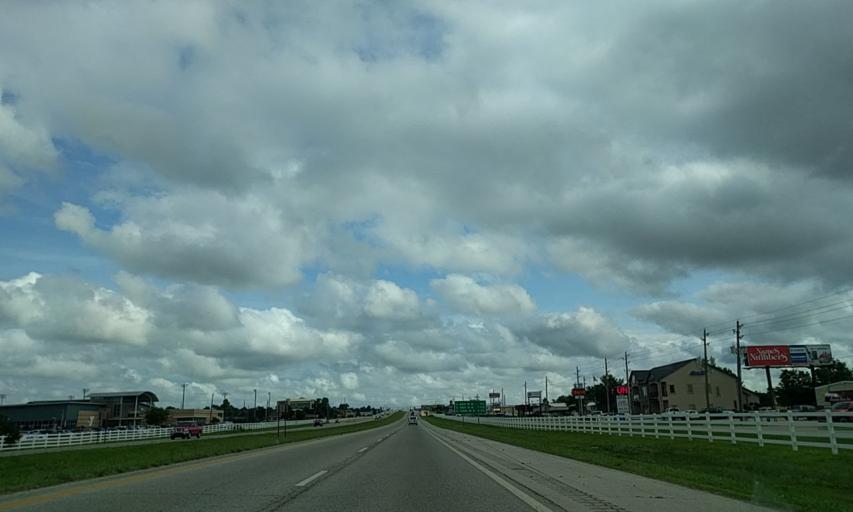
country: US
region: Oklahoma
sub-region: Tulsa County
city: Owasso
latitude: 36.2711
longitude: -95.8479
